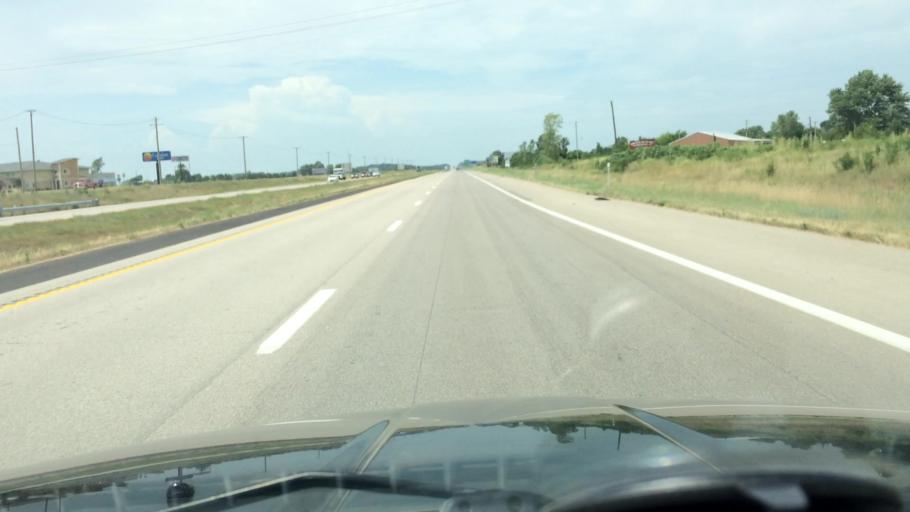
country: US
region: Missouri
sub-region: Polk County
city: Bolivar
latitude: 37.5976
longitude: -93.4359
